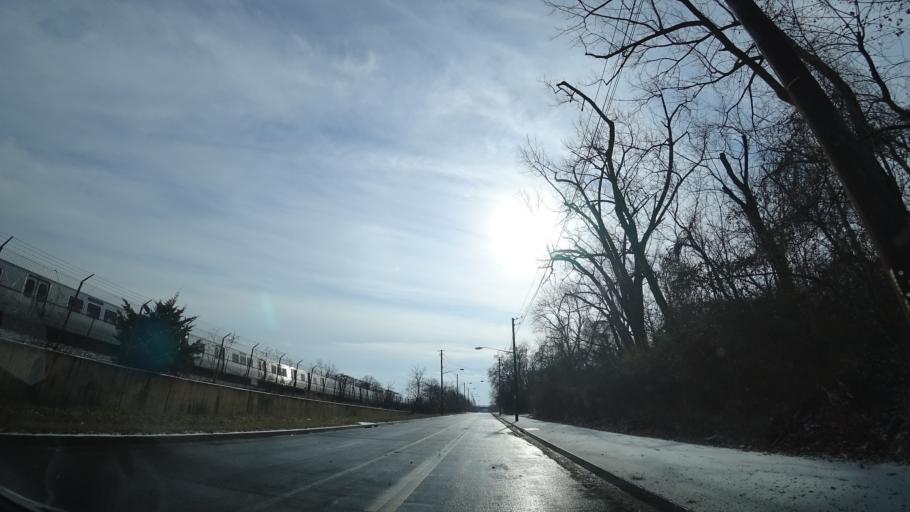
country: US
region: Maryland
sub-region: Prince George's County
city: Chillum
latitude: 38.9450
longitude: -76.9997
